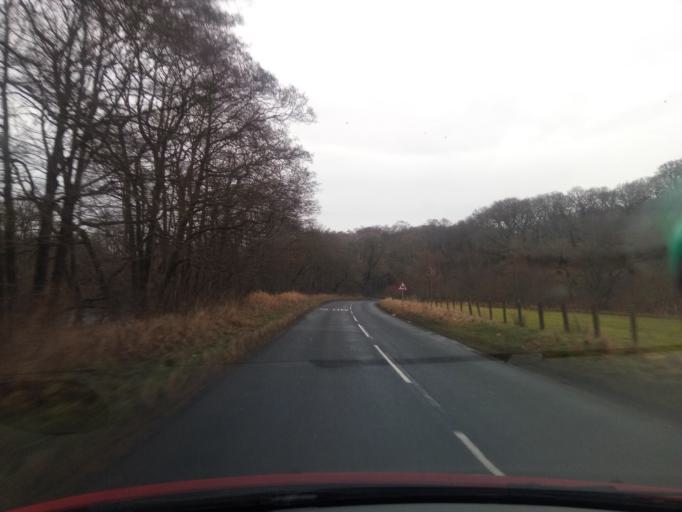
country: GB
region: England
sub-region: Northumberland
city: Rochester
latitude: 55.1663
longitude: -2.3871
